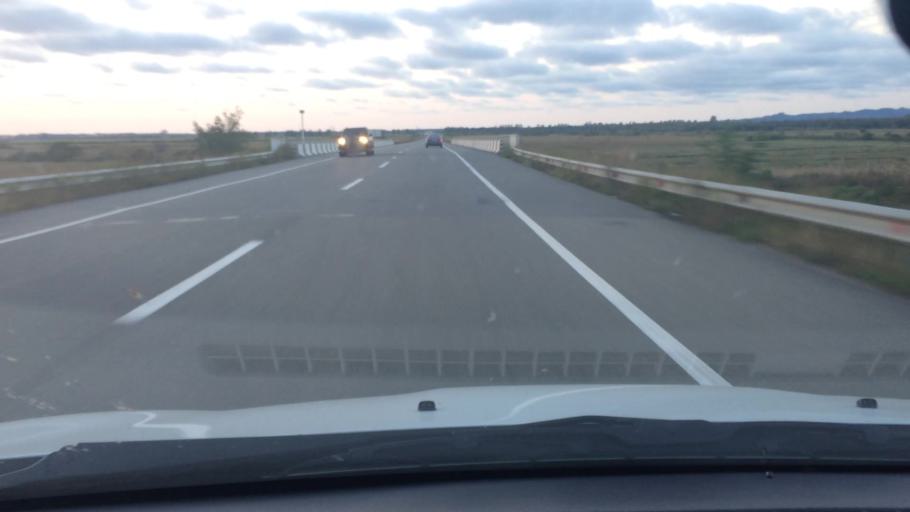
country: GE
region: Ajaria
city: Ochkhamuri
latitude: 41.8707
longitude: 41.8312
